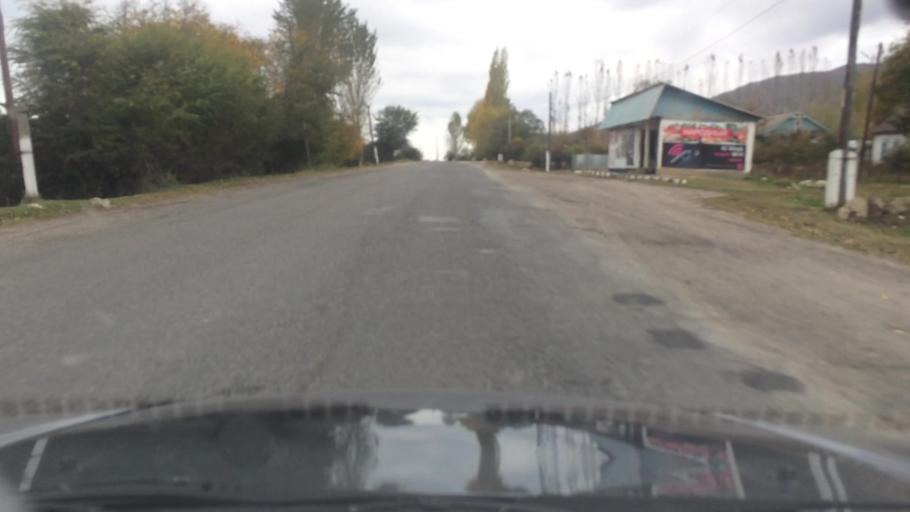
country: KG
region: Ysyk-Koel
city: Tyup
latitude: 42.7475
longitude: 78.1064
